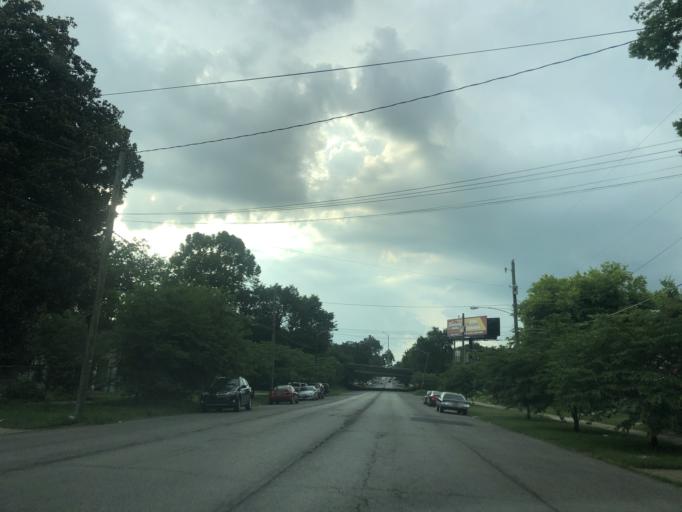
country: US
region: Tennessee
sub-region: Davidson County
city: Nashville
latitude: 36.1761
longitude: -86.7993
